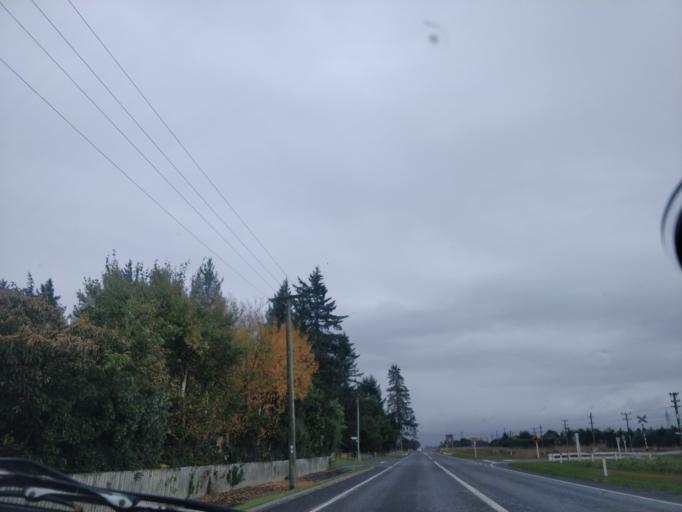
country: NZ
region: Canterbury
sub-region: Selwyn District
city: Darfield
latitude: -43.3863
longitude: 172.0150
